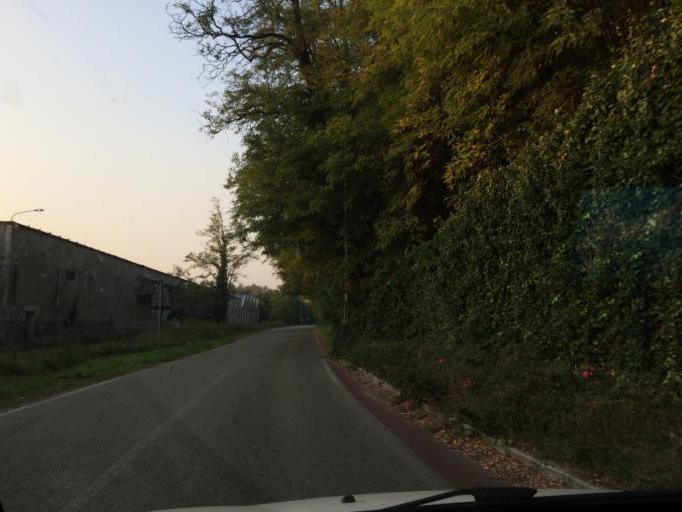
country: IT
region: Lombardy
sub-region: Provincia di Varese
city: Solbiate Olona
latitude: 45.6537
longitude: 8.8912
